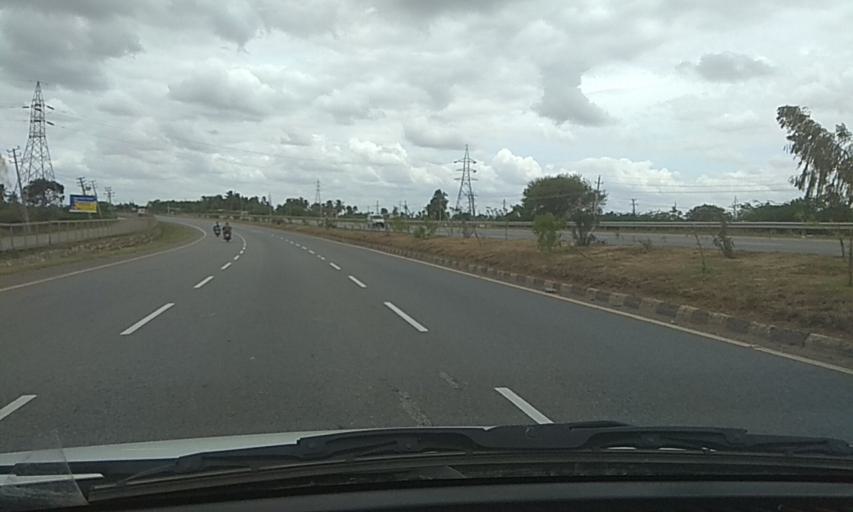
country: IN
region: Karnataka
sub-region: Chitradurga
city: Hiriyur
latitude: 13.8459
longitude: 76.7276
